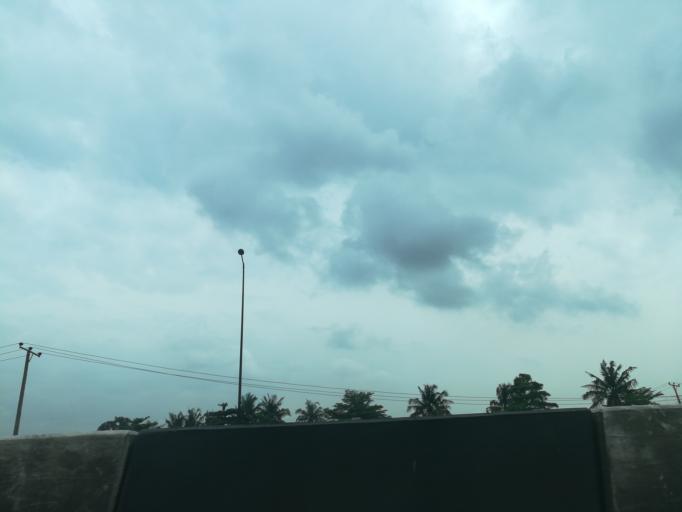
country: NG
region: Lagos
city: Ojota
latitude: 6.6039
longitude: 3.4028
